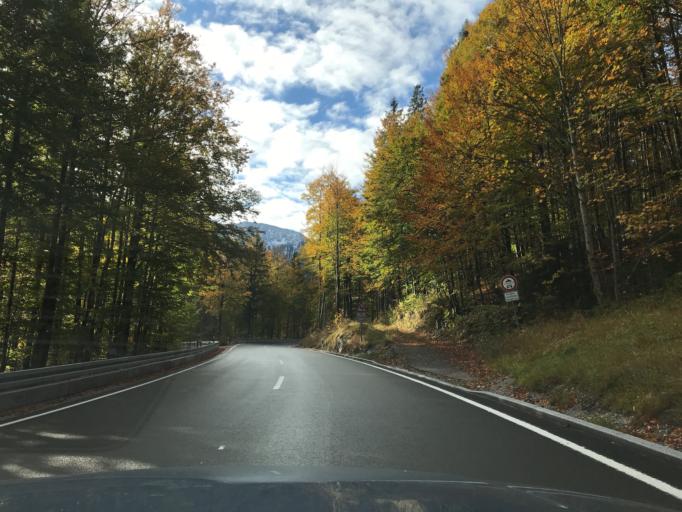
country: DE
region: Bavaria
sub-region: Upper Bavaria
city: Lenggries
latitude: 47.5819
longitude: 11.5469
